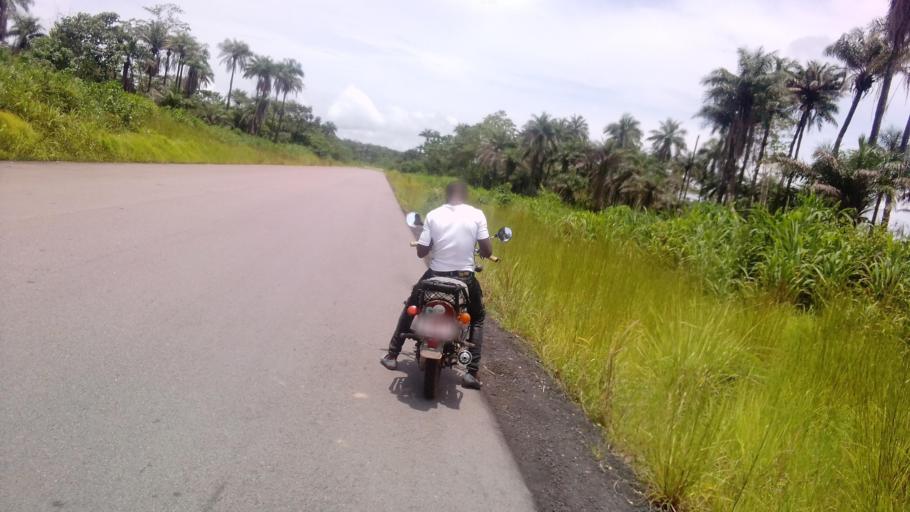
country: SL
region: Northern Province
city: Makeni
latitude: 9.0546
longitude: -12.1747
